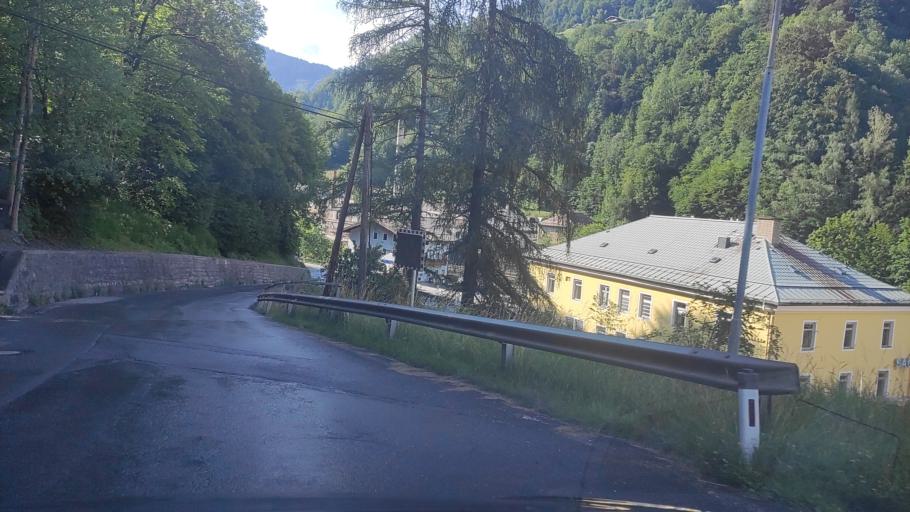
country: AT
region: Salzburg
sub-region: Politischer Bezirk Zell am See
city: Lend
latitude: 47.2967
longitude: 13.0502
